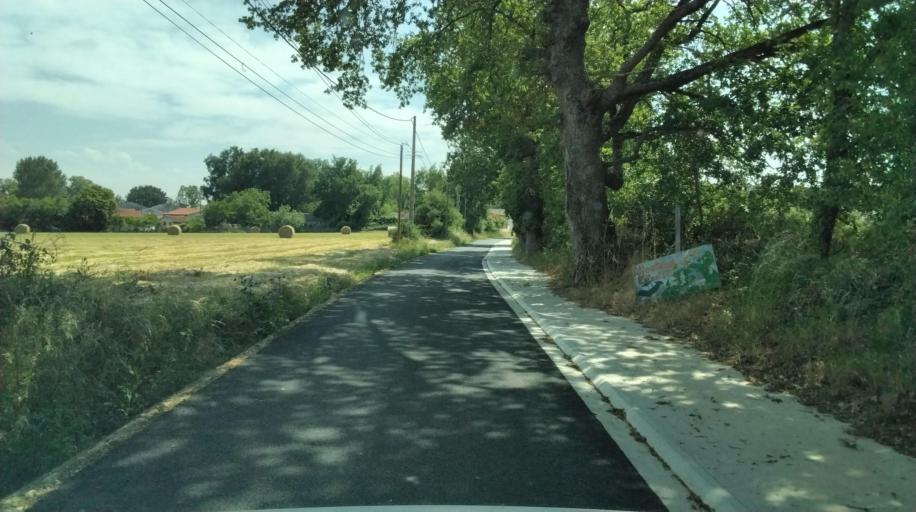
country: FR
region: Midi-Pyrenees
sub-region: Departement de la Haute-Garonne
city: Rieumes
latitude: 43.4159
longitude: 1.1272
